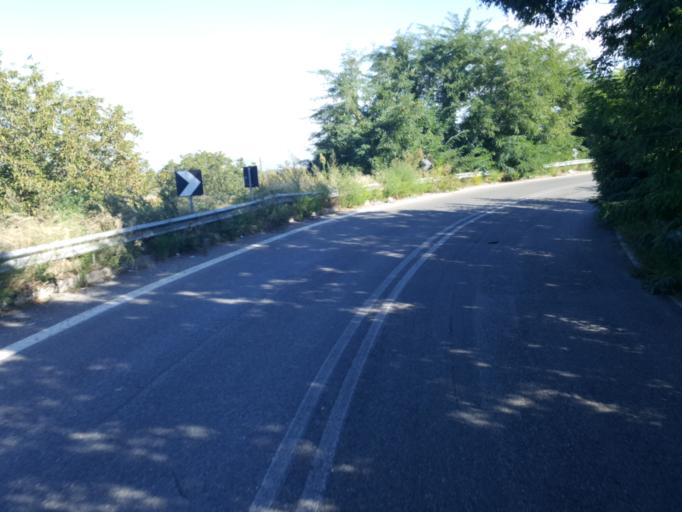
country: IT
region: Campania
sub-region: Provincia di Napoli
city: Crispano
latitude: 40.9684
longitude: 14.2896
